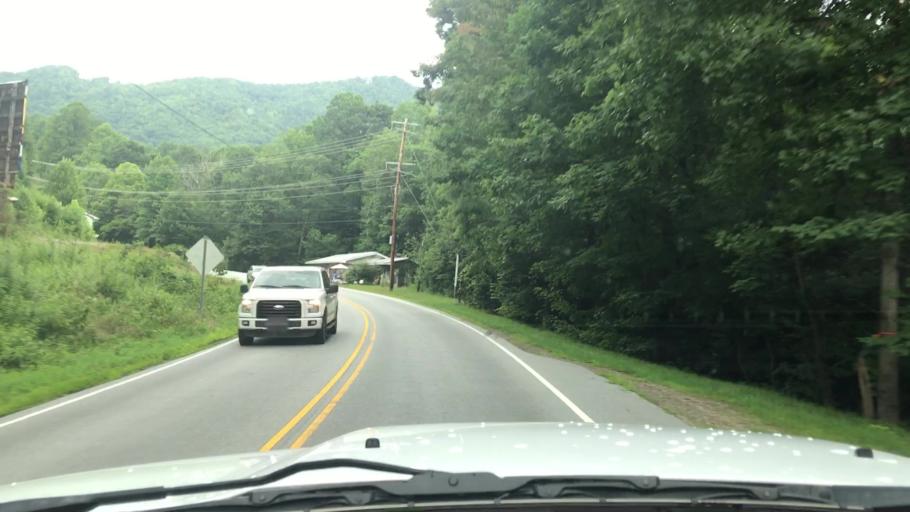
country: US
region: North Carolina
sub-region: Haywood County
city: Maggie Valley
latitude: 35.5230
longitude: -83.1126
